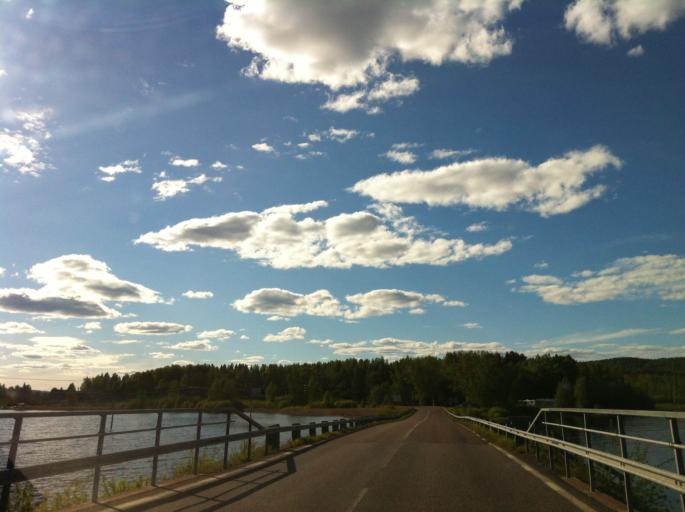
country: SE
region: Dalarna
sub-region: Leksand Municipality
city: Leksand
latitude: 60.7600
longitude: 14.9397
